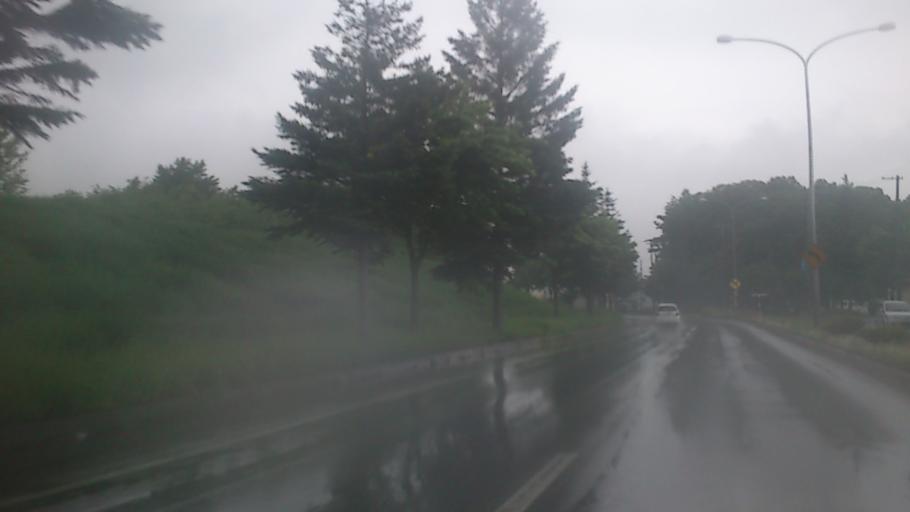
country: JP
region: Hokkaido
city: Obihiro
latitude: 42.9063
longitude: 143.1391
